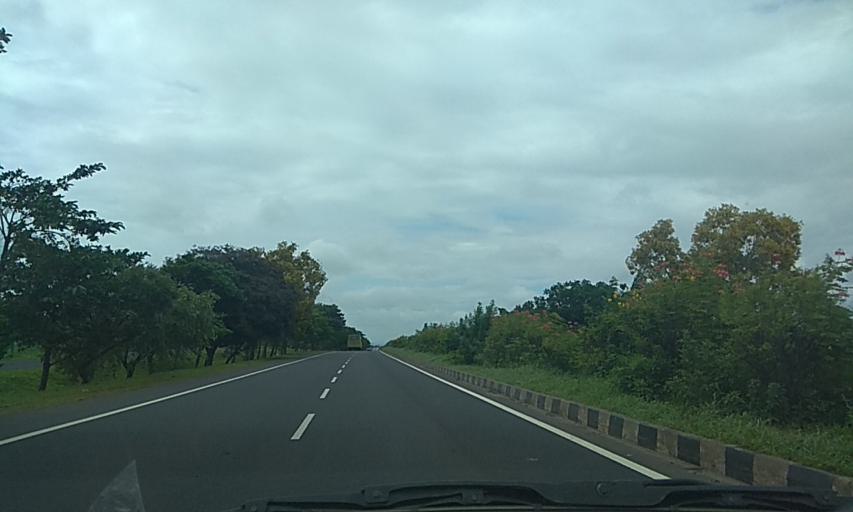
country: IN
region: Maharashtra
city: Nipani
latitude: 16.3710
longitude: 74.3999
